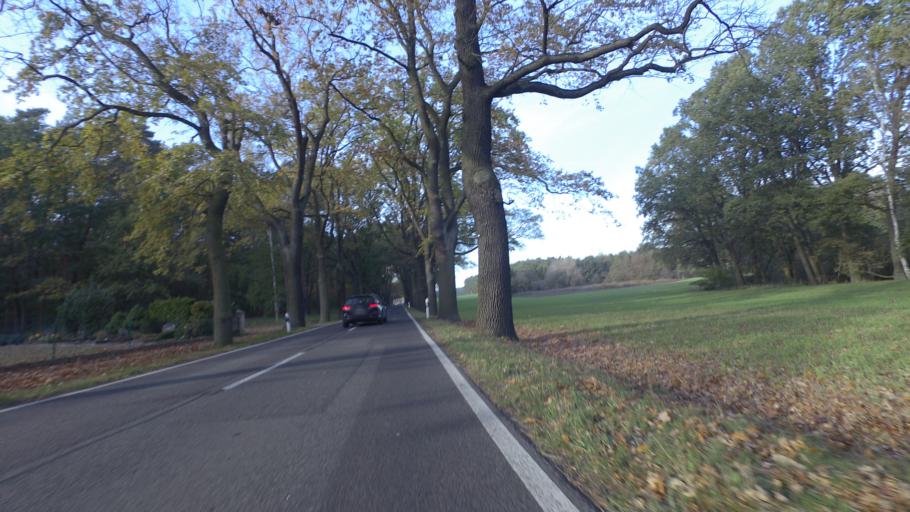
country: DE
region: Brandenburg
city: Sperenberg
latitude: 52.1924
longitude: 13.3189
